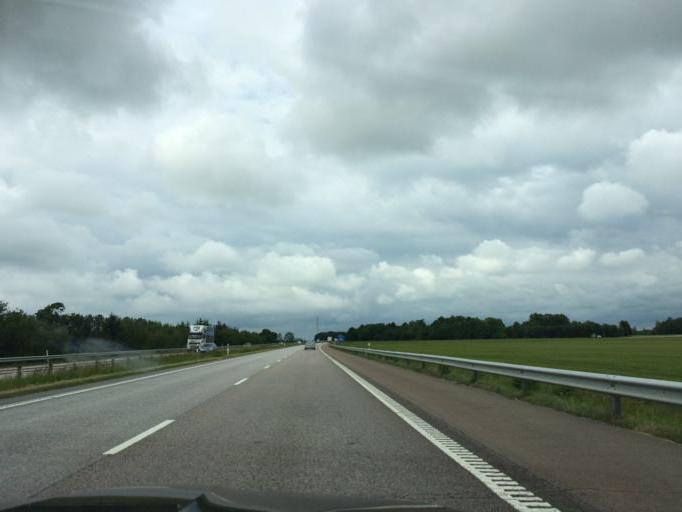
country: SE
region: Skane
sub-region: Angelholms Kommun
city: Strovelstorp
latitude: 56.1718
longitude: 12.8464
